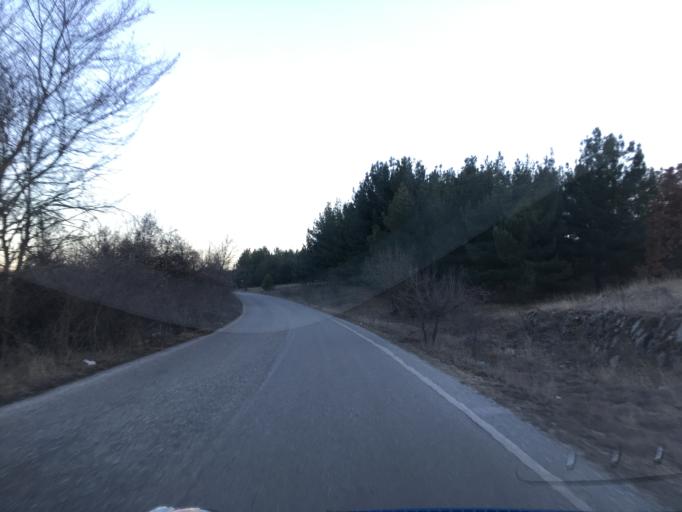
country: GR
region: West Macedonia
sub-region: Nomos Kozanis
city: Koila
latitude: 40.3257
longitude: 21.8130
